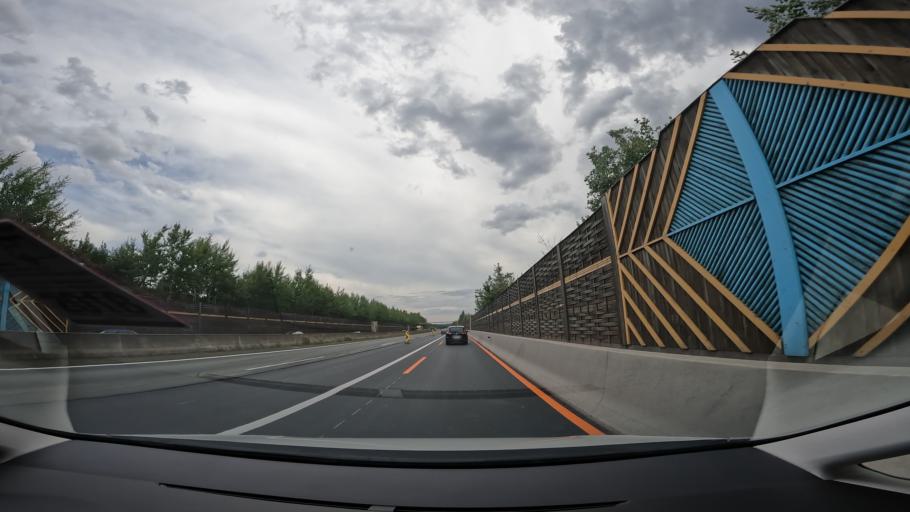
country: AT
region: Styria
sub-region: Politischer Bezirk Hartberg-Fuerstenfeld
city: Sebersdorf
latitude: 47.2363
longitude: 15.9929
